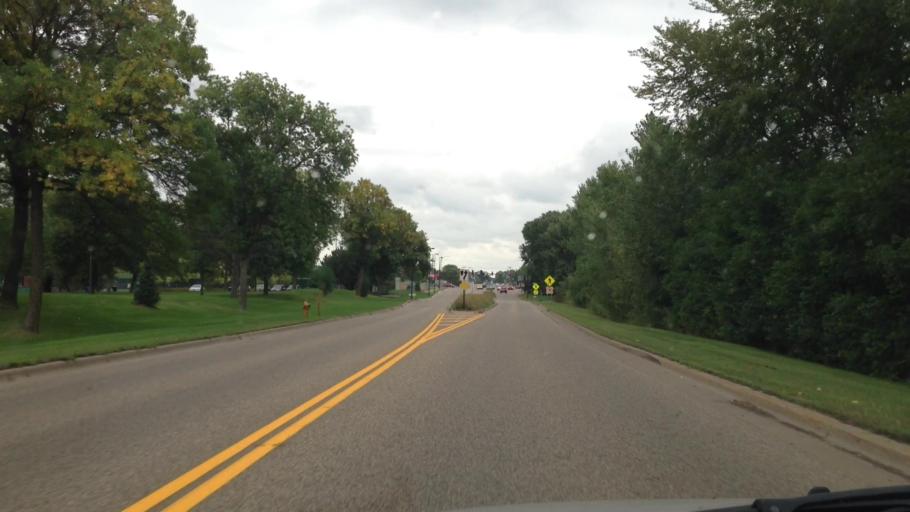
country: US
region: Minnesota
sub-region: Hennepin County
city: Golden Valley
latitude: 44.9802
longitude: -93.3803
